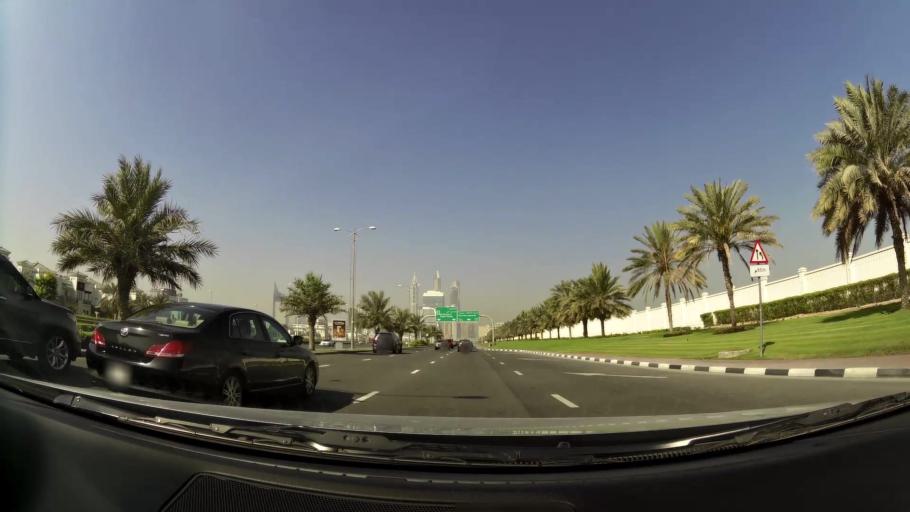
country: AE
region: Dubai
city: Dubai
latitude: 25.1076
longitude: 55.1641
